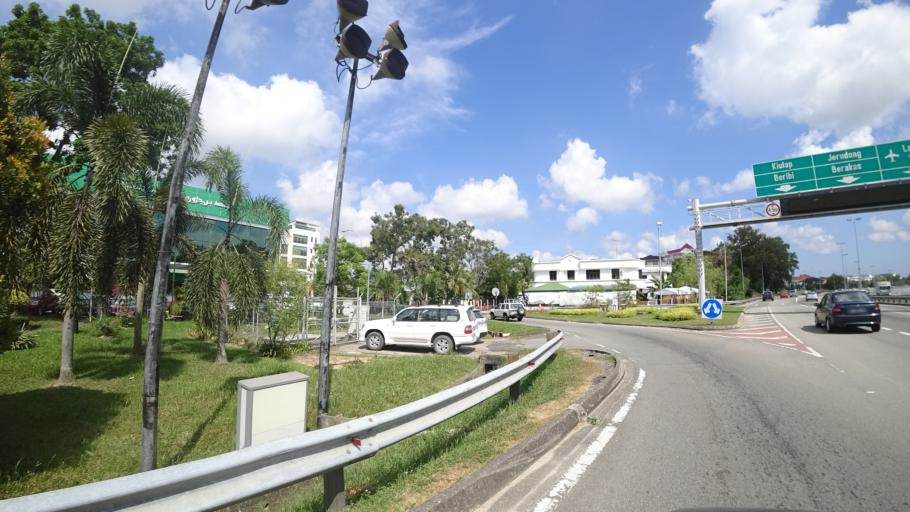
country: BN
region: Brunei and Muara
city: Bandar Seri Begawan
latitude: 4.8972
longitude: 114.9213
